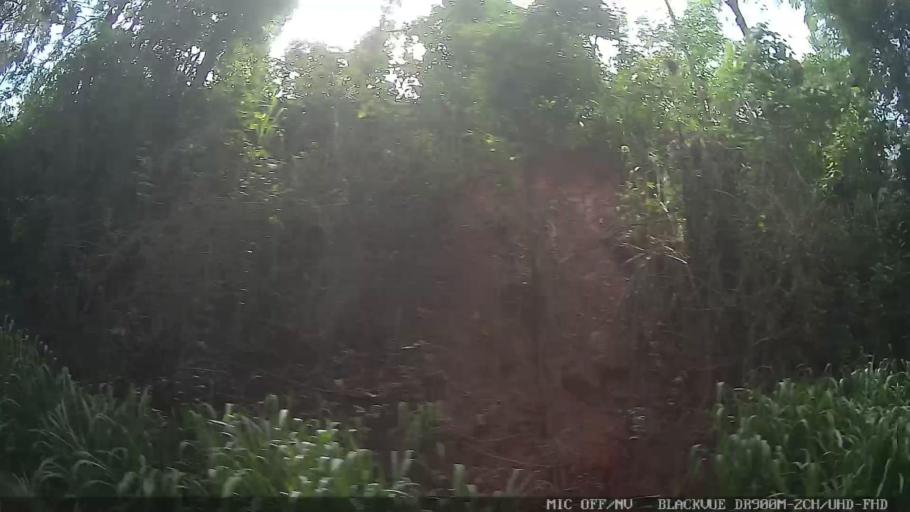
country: BR
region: Sao Paulo
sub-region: Mogi das Cruzes
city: Mogi das Cruzes
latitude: -23.4805
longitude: -46.2577
